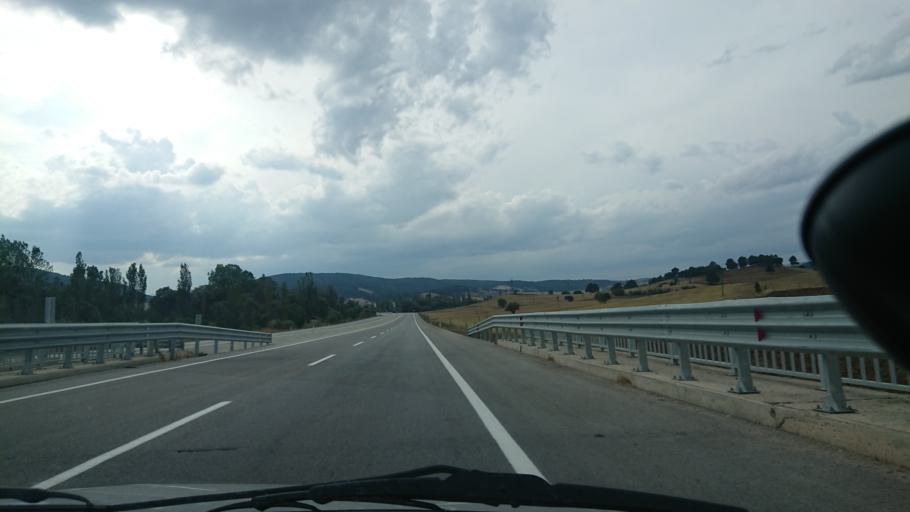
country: TR
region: Kuetahya
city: Cavdarhisar
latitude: 39.1053
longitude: 29.5030
